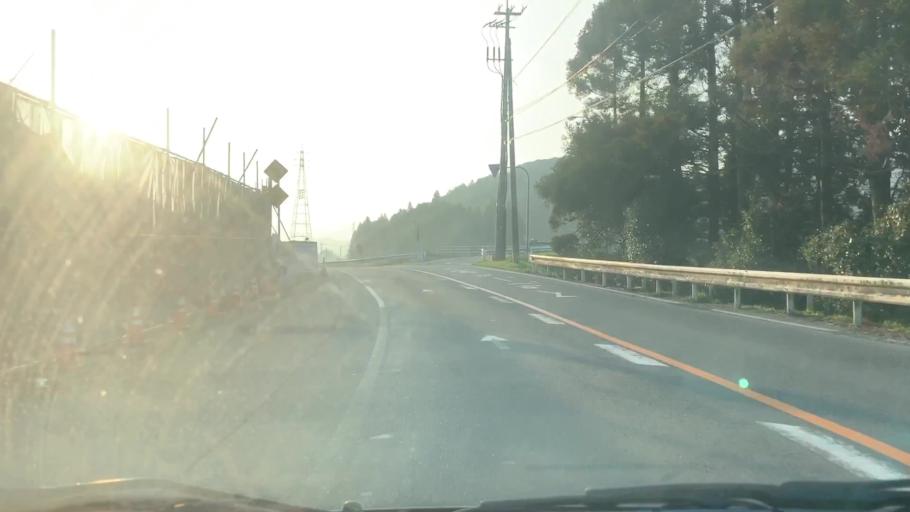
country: JP
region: Saga Prefecture
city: Takeocho-takeo
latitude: 33.2725
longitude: 130.1132
